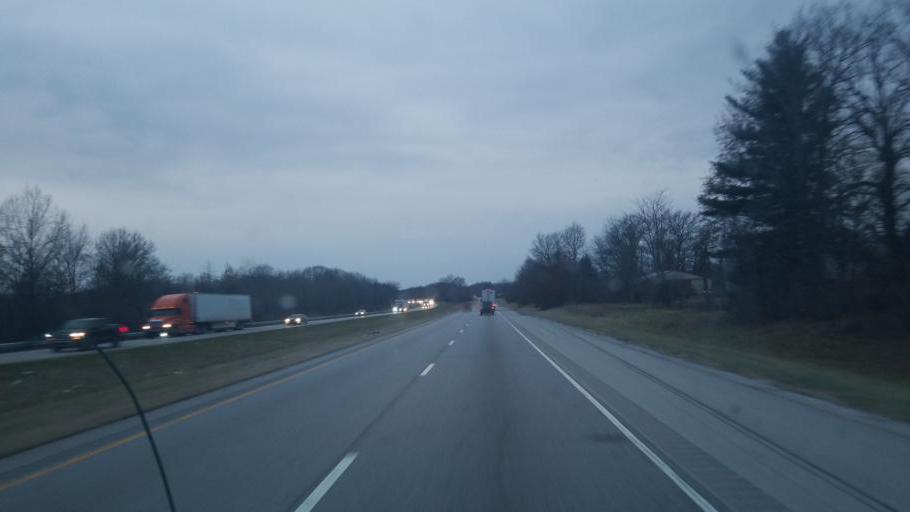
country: US
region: Indiana
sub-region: Vigo County
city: Seelyville
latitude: 39.4460
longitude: -87.2446
